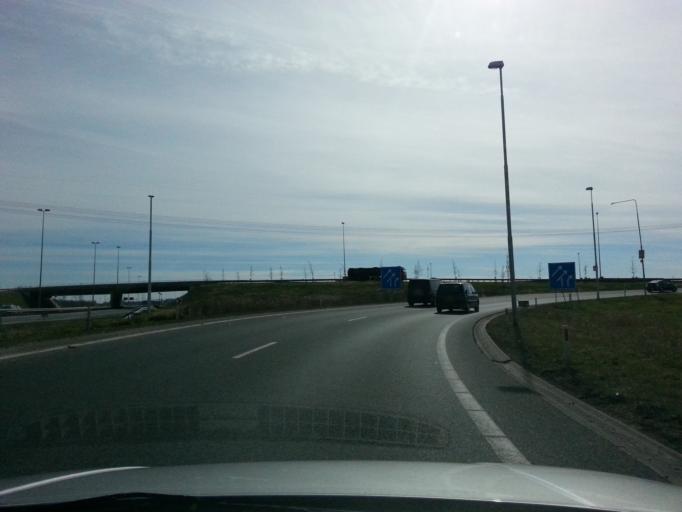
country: NL
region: Groningen
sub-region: Gemeente Groningen
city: Oosterpark
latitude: 53.2188
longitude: 6.6168
